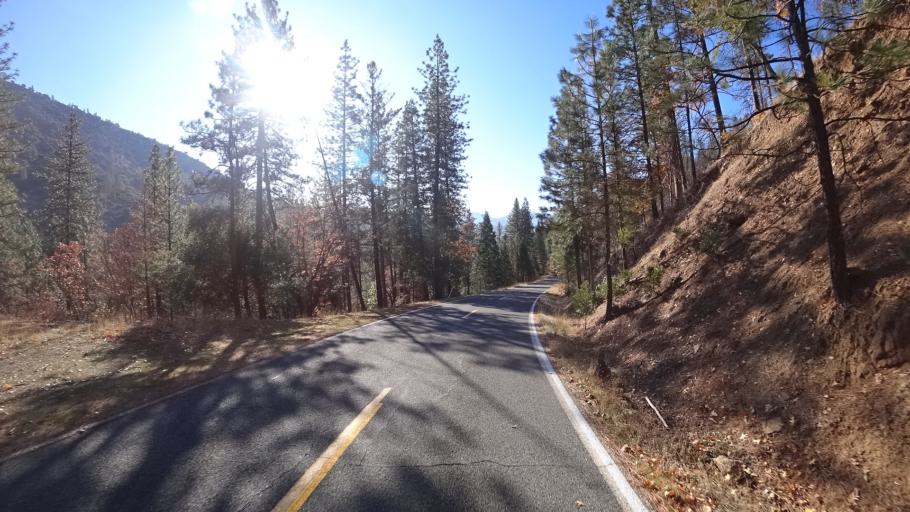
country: US
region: California
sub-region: Siskiyou County
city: Yreka
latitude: 41.8876
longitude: -122.8233
